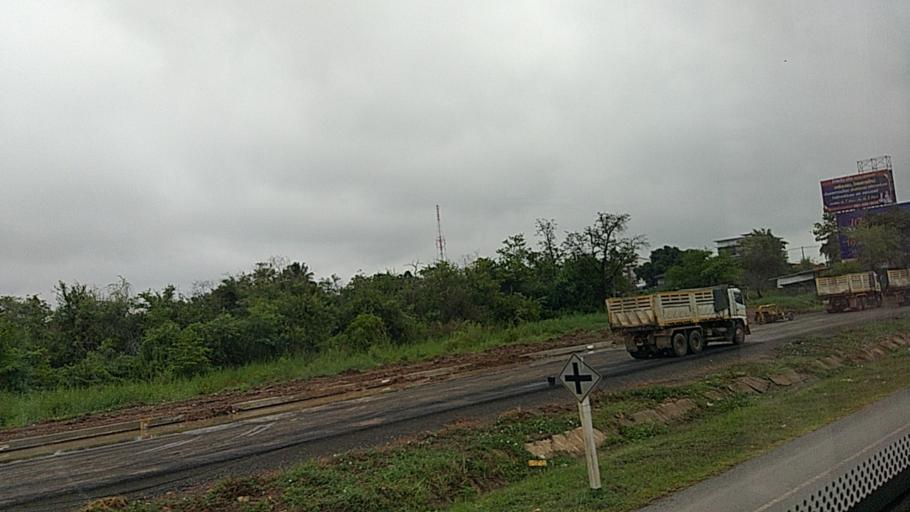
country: TH
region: Nakhon Ratchasima
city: Nakhon Ratchasima
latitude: 14.9951
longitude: 102.0879
